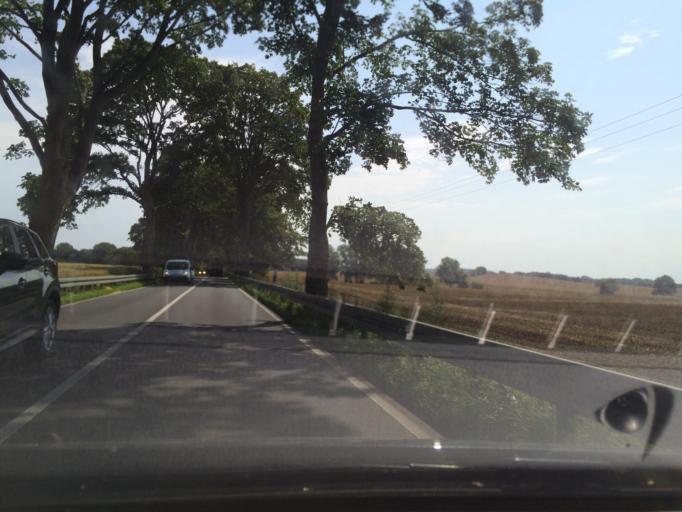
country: DE
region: Mecklenburg-Vorpommern
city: Putbus
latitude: 54.4046
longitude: 13.4823
